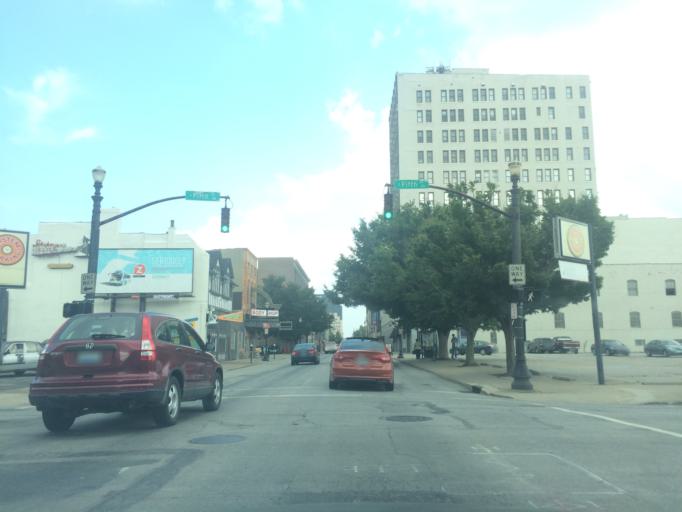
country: US
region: Kentucky
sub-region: Jefferson County
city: Louisville
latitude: 38.2491
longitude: -85.7597
